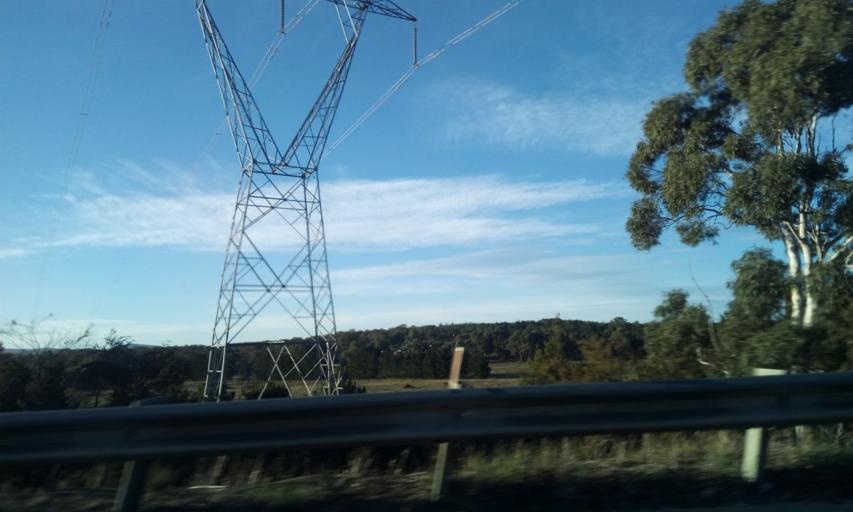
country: AU
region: New South Wales
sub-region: Yass Valley
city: Gundaroo
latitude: -35.1594
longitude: 149.3219
